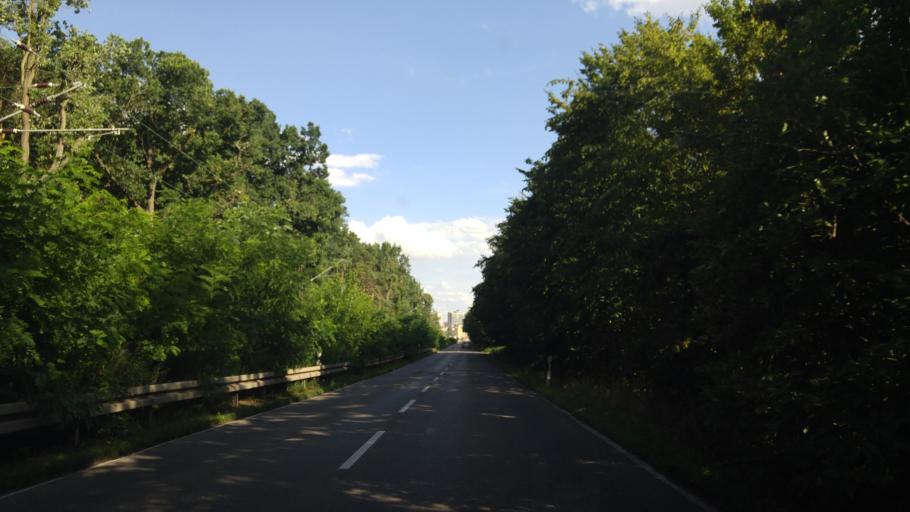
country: DE
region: Saxony-Anhalt
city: Halle Neustadt
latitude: 51.4917
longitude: 11.8999
